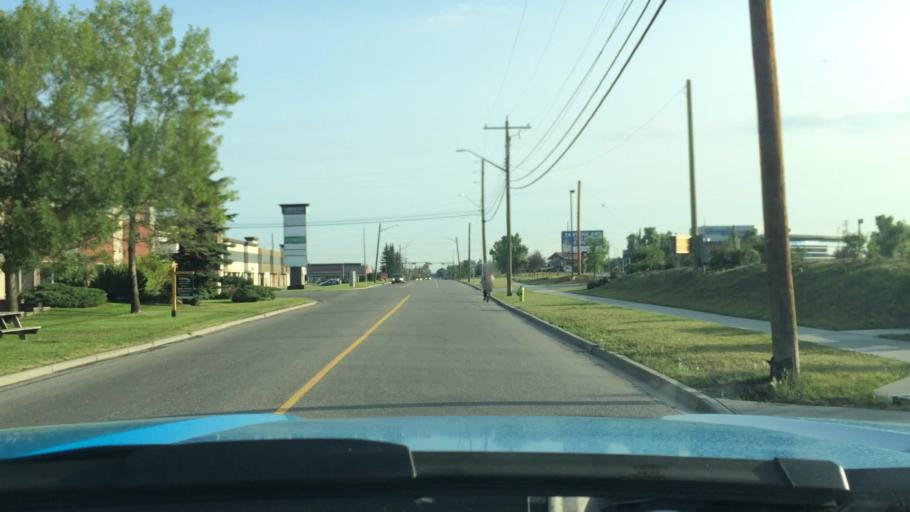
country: CA
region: Alberta
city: Calgary
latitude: 51.0790
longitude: -114.0051
